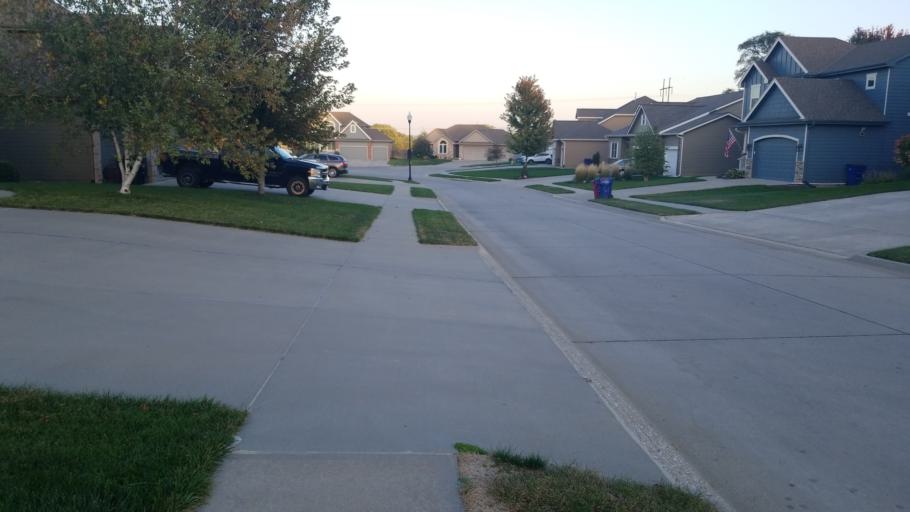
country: US
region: Nebraska
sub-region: Sarpy County
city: Offutt Air Force Base
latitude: 41.1436
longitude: -95.9787
